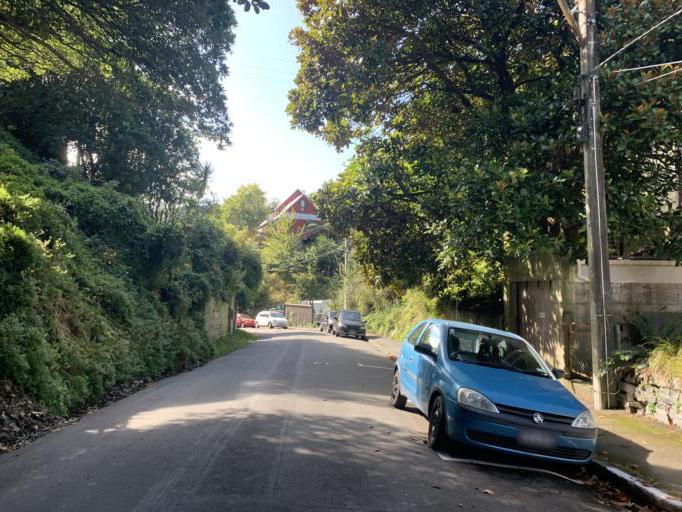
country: NZ
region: Wellington
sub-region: Wellington City
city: Kelburn
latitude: -41.2956
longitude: 174.7580
